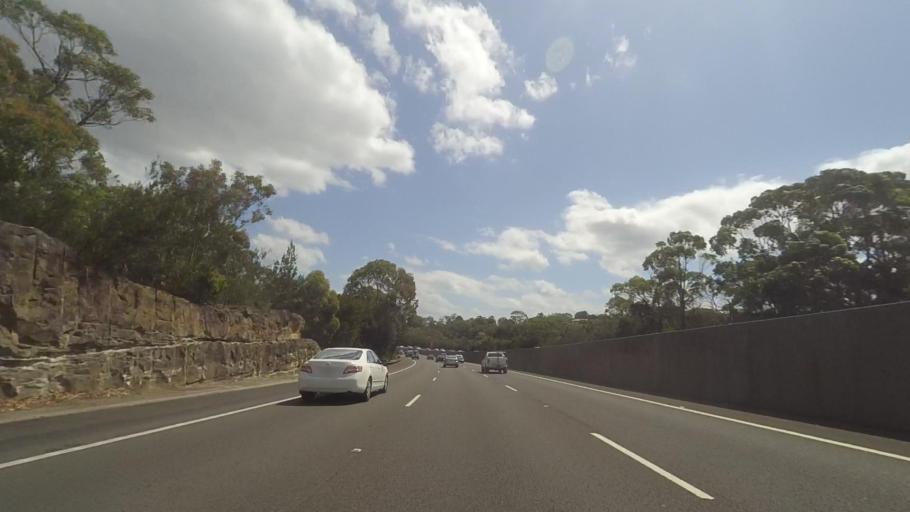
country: AU
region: New South Wales
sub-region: Hornsby Shire
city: Berowra
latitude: -33.5876
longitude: 151.1765
